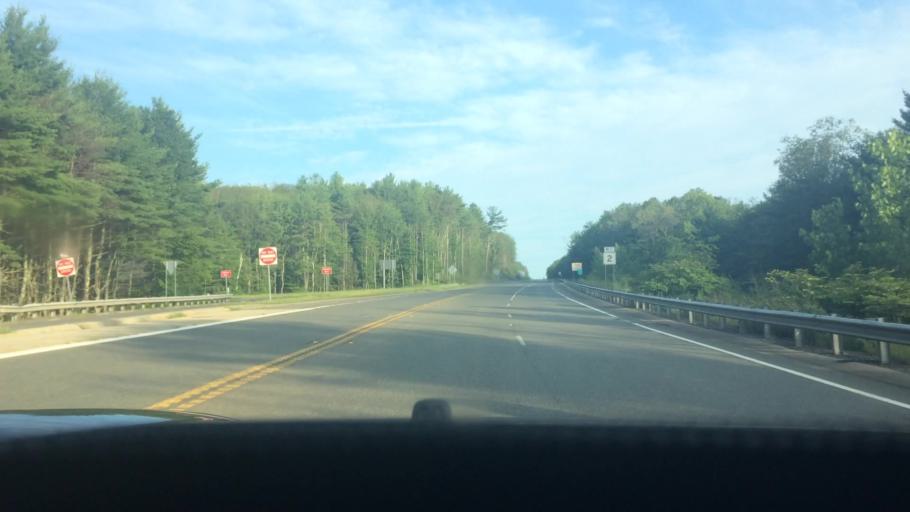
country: US
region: Massachusetts
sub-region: Franklin County
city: Orange
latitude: 42.5590
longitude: -72.3023
